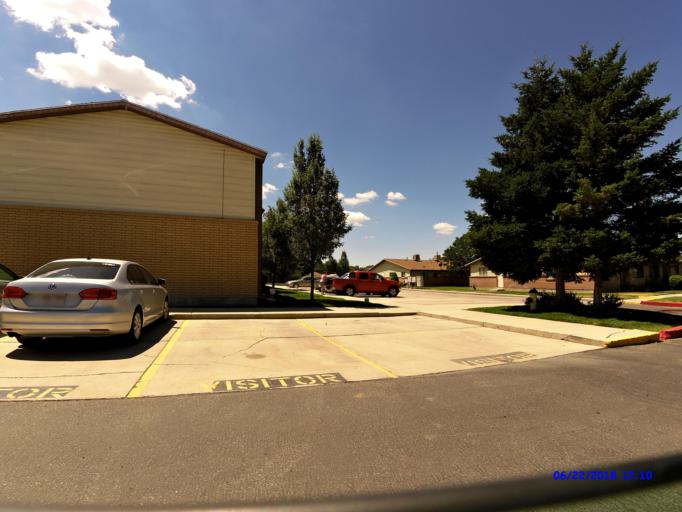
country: US
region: Utah
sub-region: Weber County
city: Ogden
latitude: 41.2404
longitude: -111.9545
